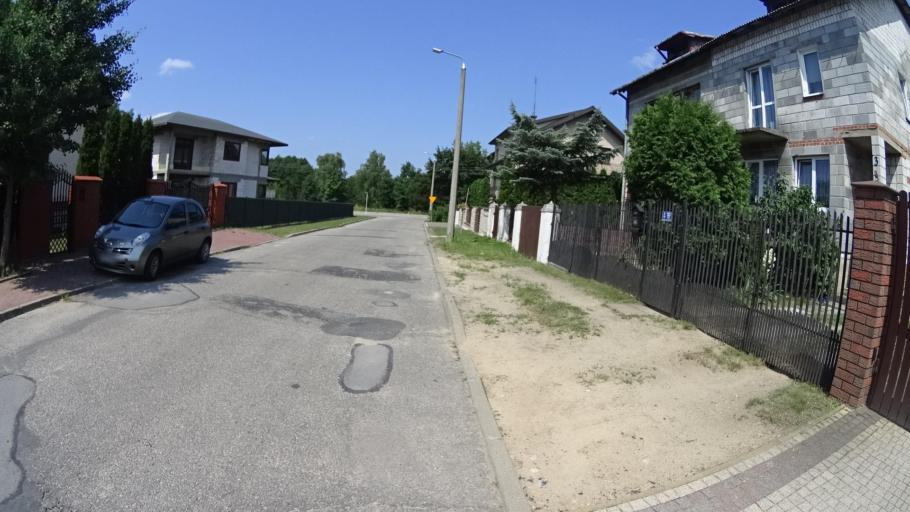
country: PL
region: Masovian Voivodeship
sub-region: Powiat bialobrzeski
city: Bialobrzegi
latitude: 51.6456
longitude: 20.9603
